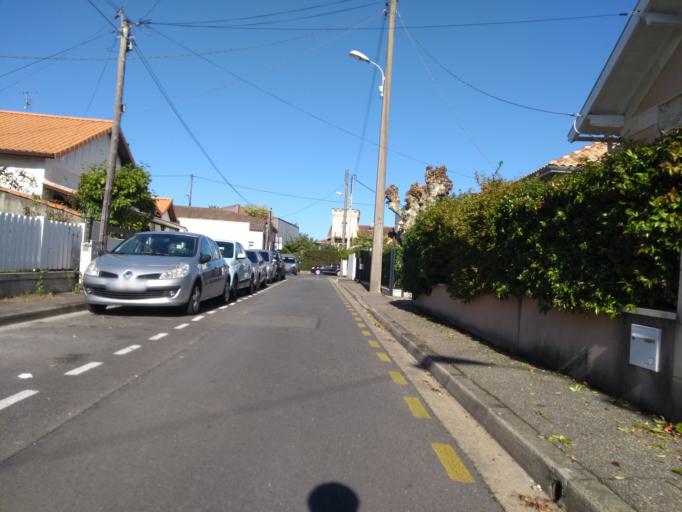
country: FR
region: Aquitaine
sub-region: Departement de la Gironde
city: Pessac
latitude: 44.8051
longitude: -0.6344
